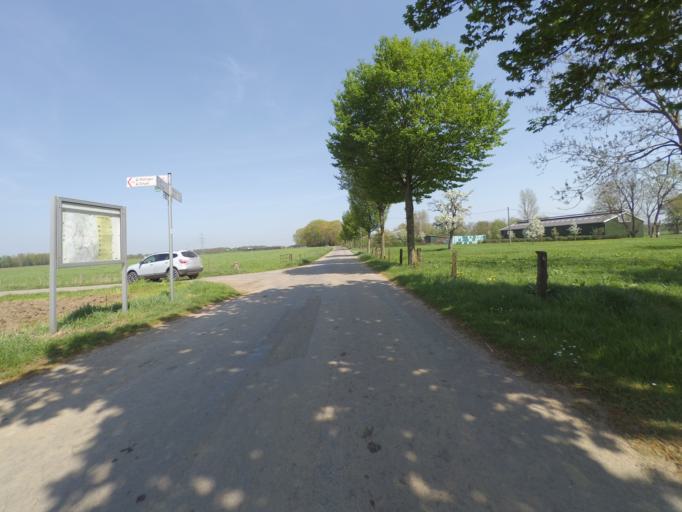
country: DE
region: North Rhine-Westphalia
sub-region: Regierungsbezirk Munster
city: Isselburg
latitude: 51.7923
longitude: 6.4536
